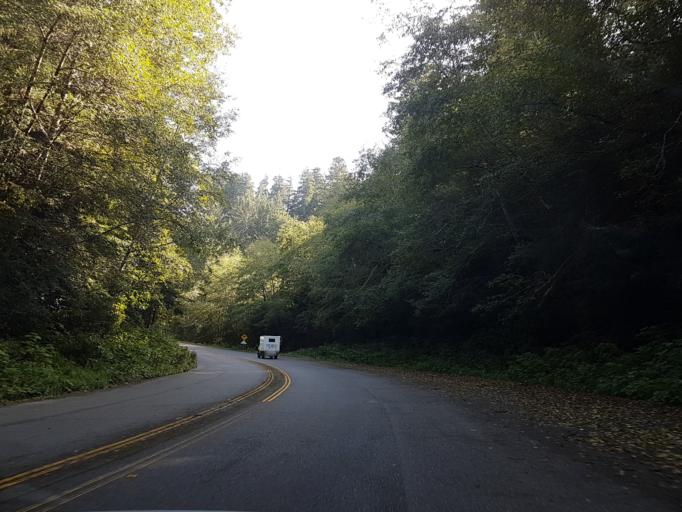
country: US
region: California
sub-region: Del Norte County
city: Bertsch-Oceanview
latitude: 41.4589
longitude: -124.0473
